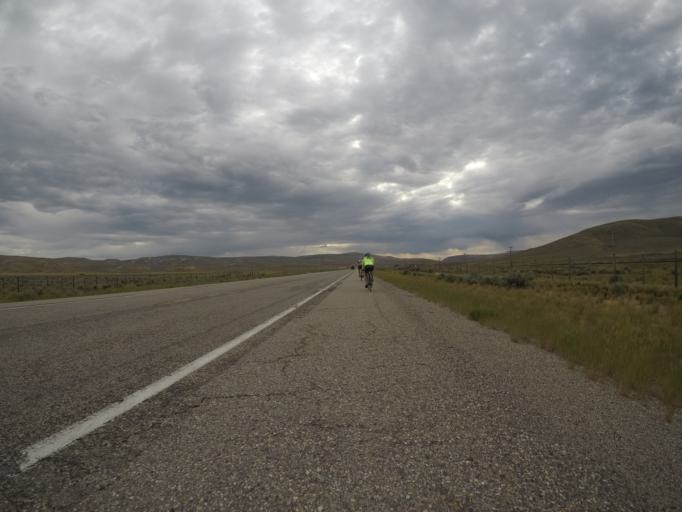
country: US
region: Utah
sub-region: Rich County
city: Randolph
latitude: 41.8235
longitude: -110.9309
